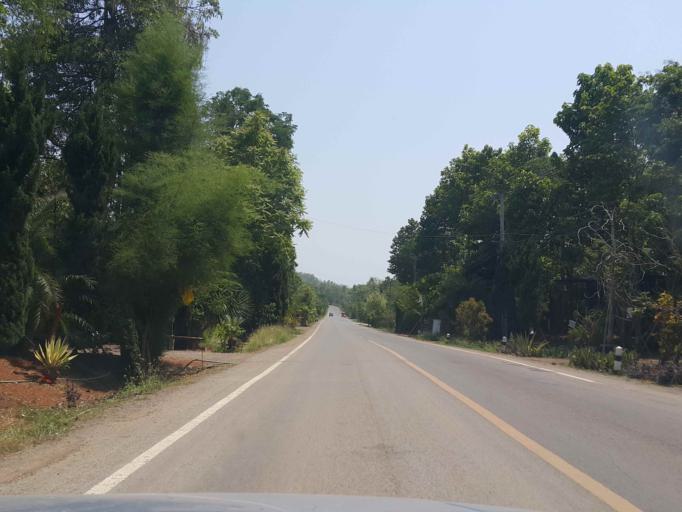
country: TH
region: Chiang Mai
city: Mae On
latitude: 18.8457
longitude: 99.2645
